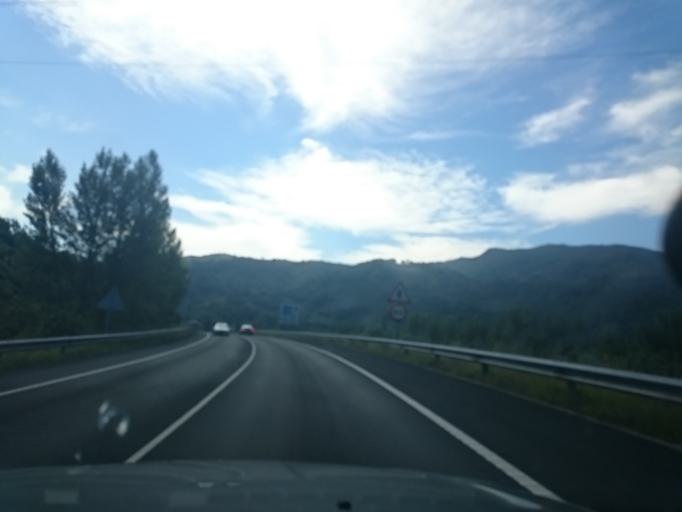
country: ES
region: Asturias
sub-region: Province of Asturias
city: Oviedo
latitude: 43.3044
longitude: -5.8303
